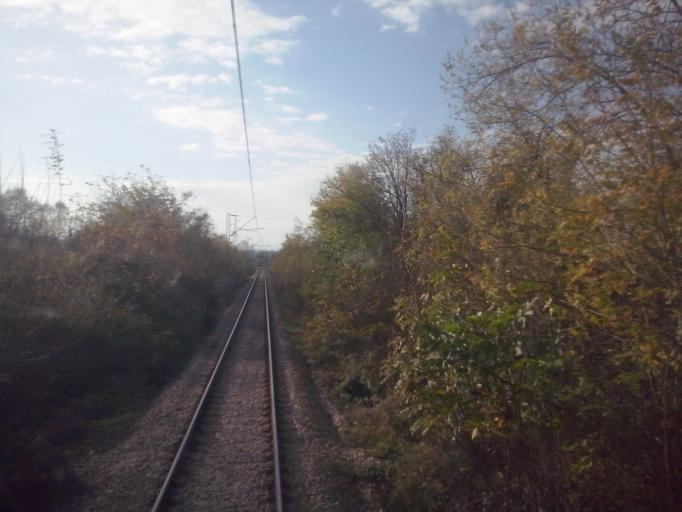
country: RS
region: Central Serbia
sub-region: Belgrade
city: Lazarevac
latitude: 44.4238
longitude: 20.2776
